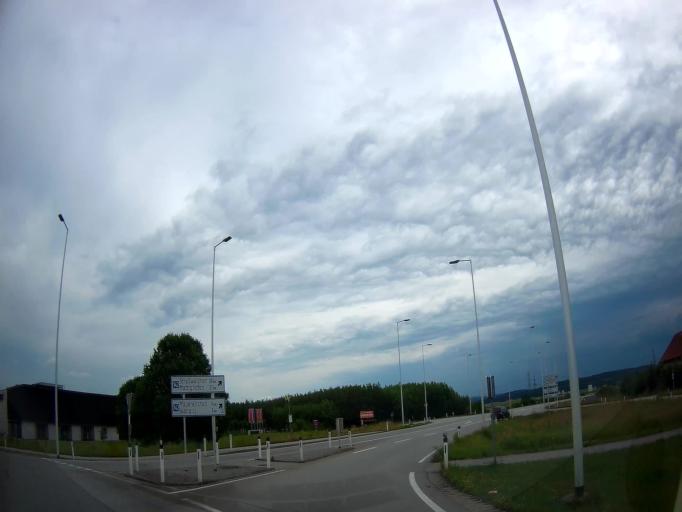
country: AT
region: Upper Austria
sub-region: Politischer Bezirk Braunau am Inn
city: Altheim
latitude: 48.2501
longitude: 13.1931
